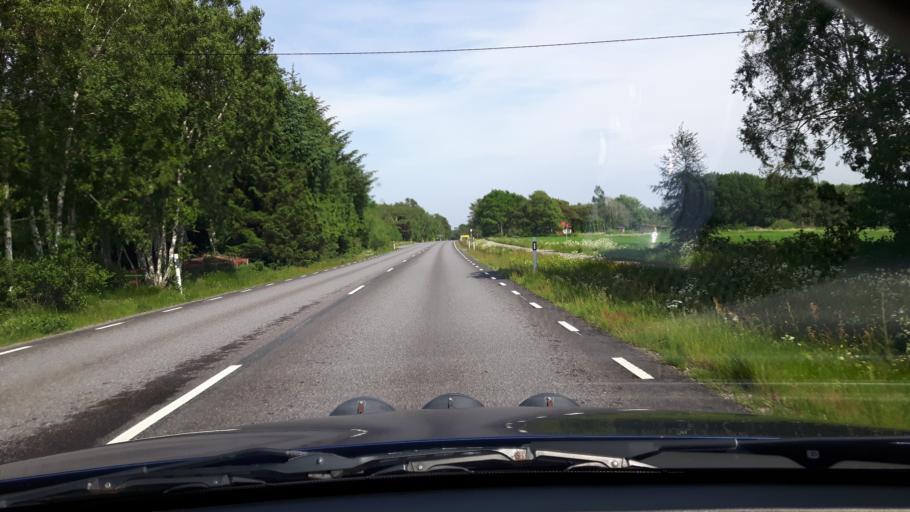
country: SE
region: Halland
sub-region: Varbergs Kommun
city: Tvaaker
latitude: 57.0483
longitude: 12.3464
